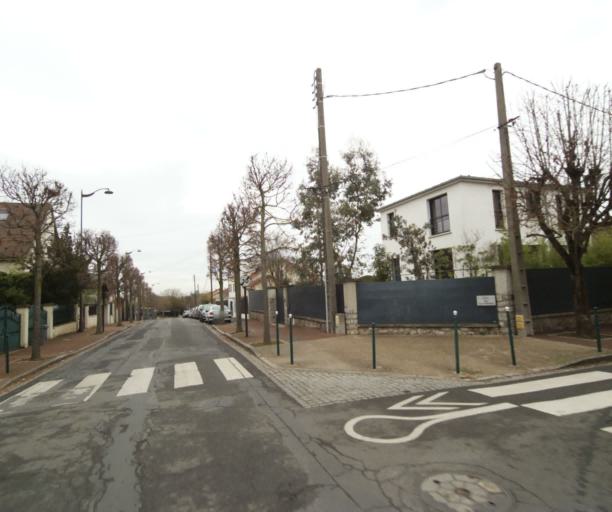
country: FR
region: Ile-de-France
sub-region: Departement des Hauts-de-Seine
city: Rueil-Malmaison
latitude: 48.8653
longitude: 2.1845
